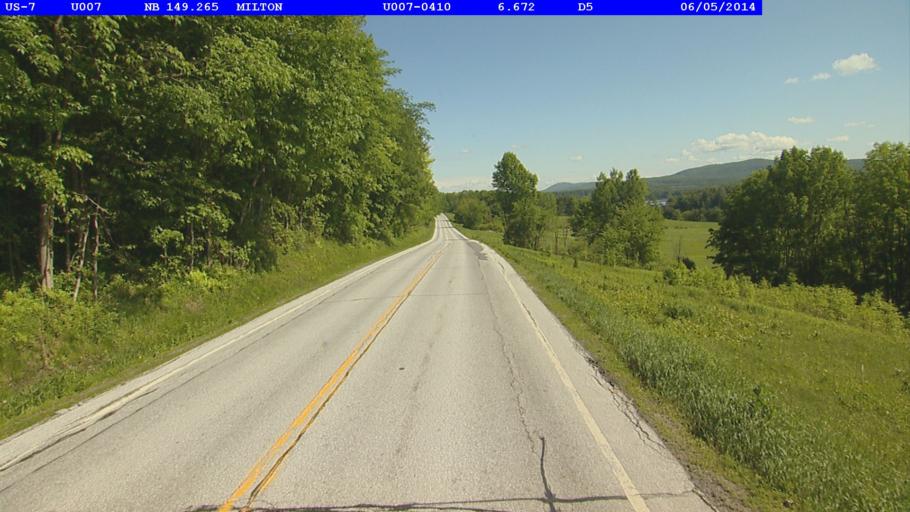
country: US
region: Vermont
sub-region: Chittenden County
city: Milton
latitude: 44.6626
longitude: -73.1116
